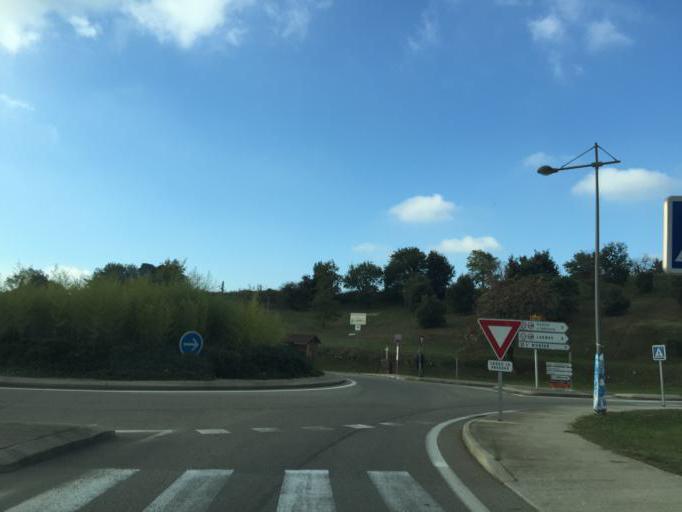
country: FR
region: Rhone-Alpes
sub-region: Departement de l'Ardeche
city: Bourg-Saint-Andeol
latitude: 44.4303
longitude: 4.6503
